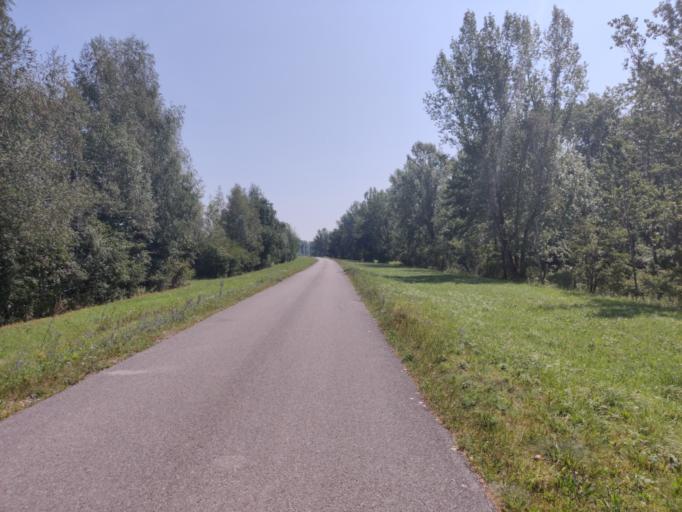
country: AT
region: Upper Austria
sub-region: Politischer Bezirk Urfahr-Umgebung
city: Feldkirchen an der Donau
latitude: 48.3258
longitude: 14.0433
